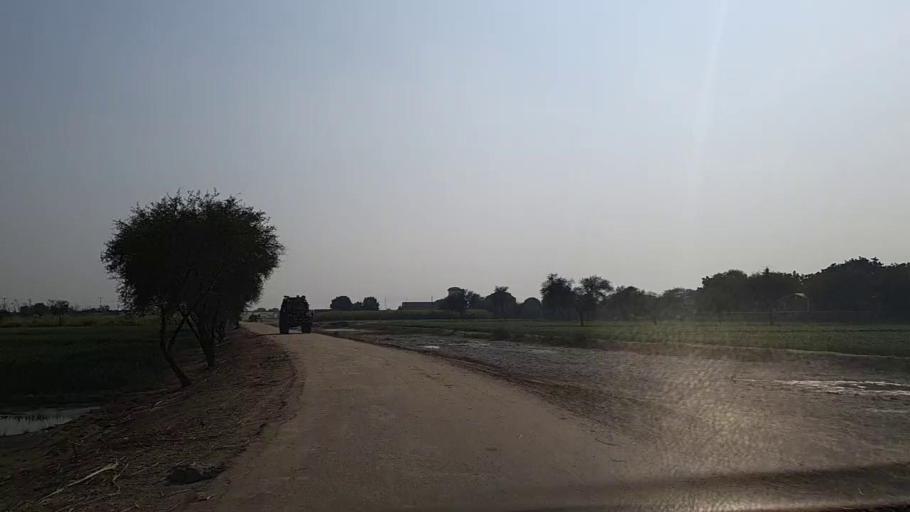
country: PK
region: Sindh
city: Daur
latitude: 26.4009
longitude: 68.4174
